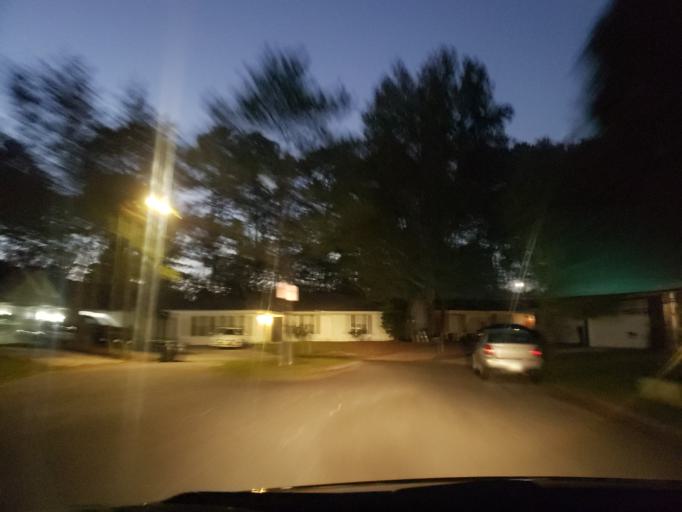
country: US
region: Georgia
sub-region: Chatham County
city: Isle of Hope
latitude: 31.9945
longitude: -81.0683
